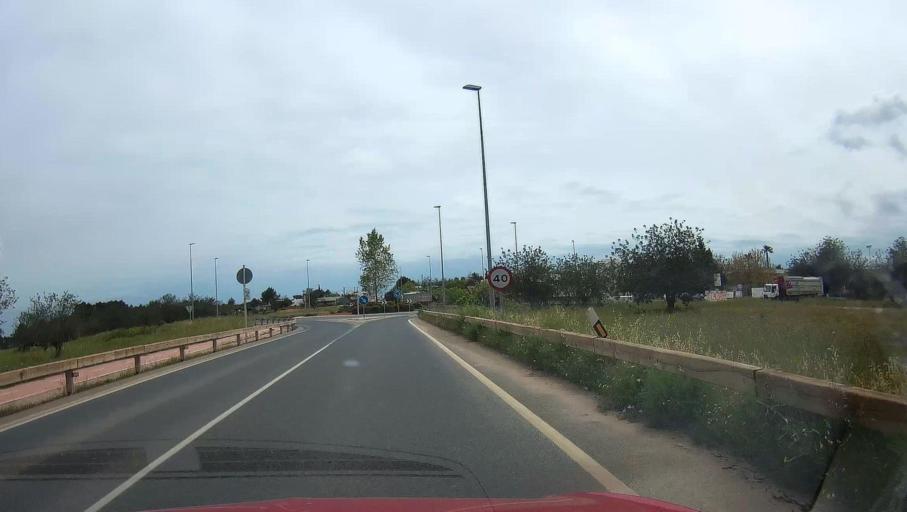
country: ES
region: Balearic Islands
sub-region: Illes Balears
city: Ibiza
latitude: 39.0022
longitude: 1.4296
